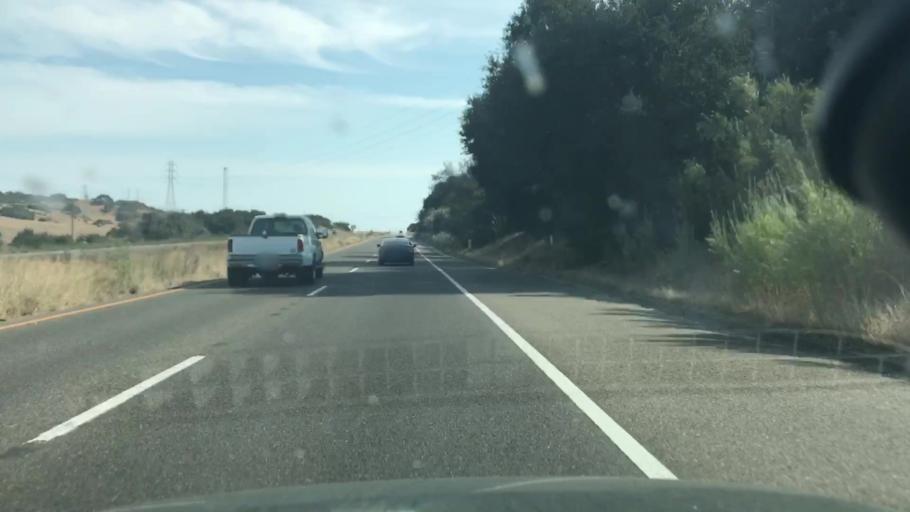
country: US
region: California
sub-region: Santa Barbara County
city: Orcutt
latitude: 34.8343
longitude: -120.4514
